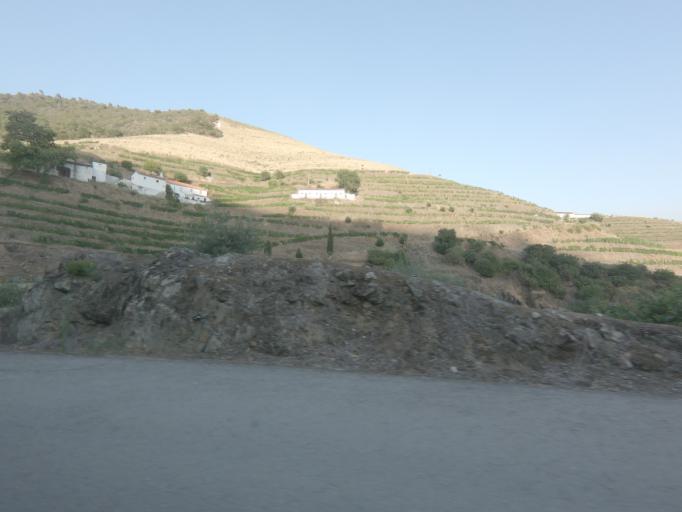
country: PT
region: Vila Real
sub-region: Sabrosa
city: Vilela
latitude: 41.1678
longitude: -7.6253
